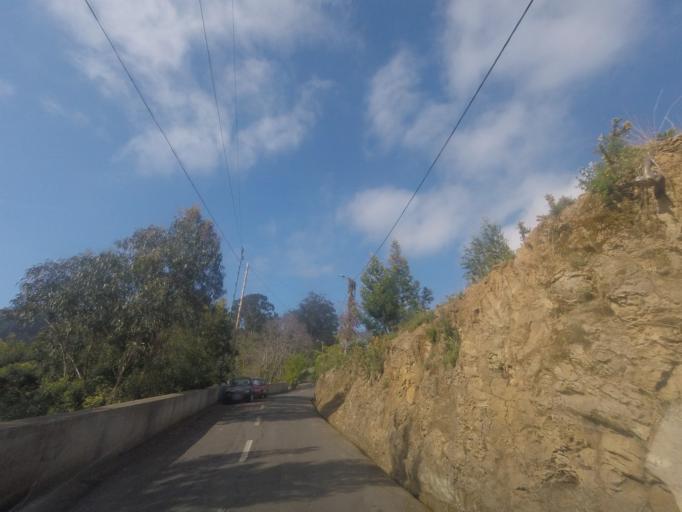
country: PT
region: Madeira
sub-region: Camara de Lobos
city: Curral das Freiras
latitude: 32.6785
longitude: -16.9537
